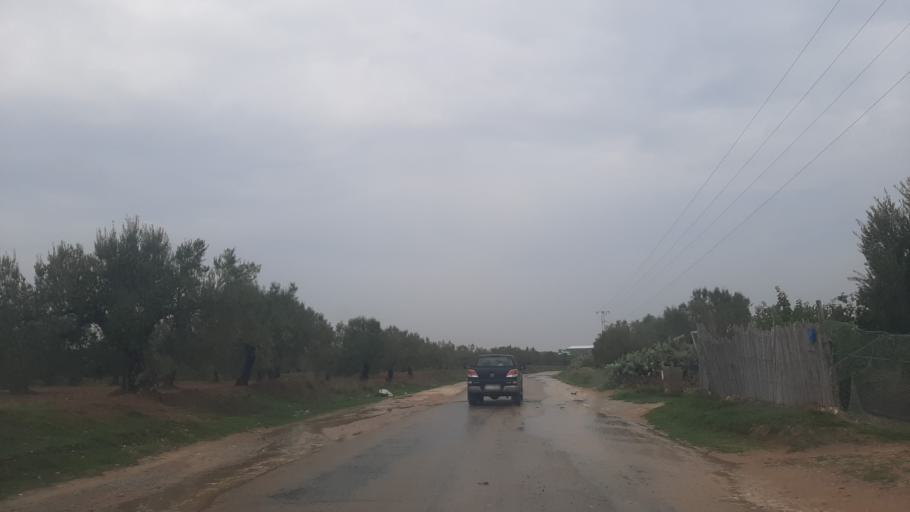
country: TN
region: Al Munastir
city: Sidi Bin Nur
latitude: 35.4723
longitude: 10.8837
